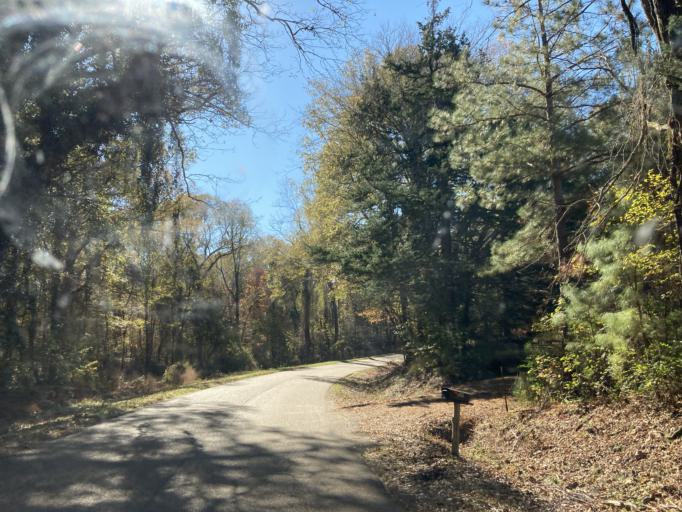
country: US
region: Mississippi
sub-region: Hinds County
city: Lynchburg
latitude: 32.5796
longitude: -90.5696
